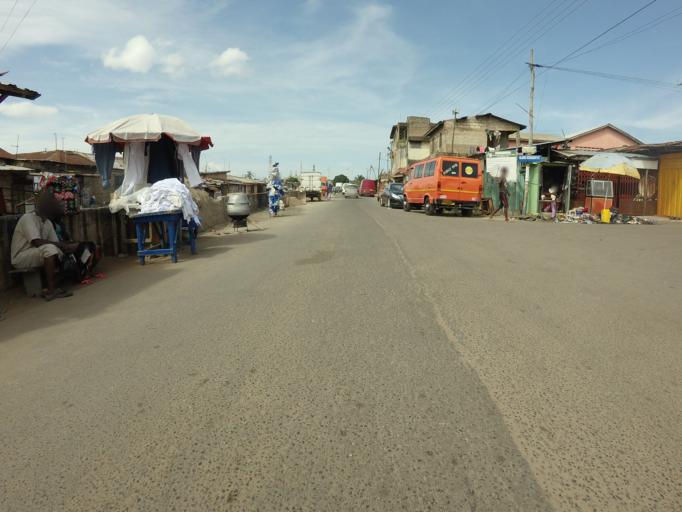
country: GH
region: Greater Accra
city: Accra
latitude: 5.5879
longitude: -0.1990
